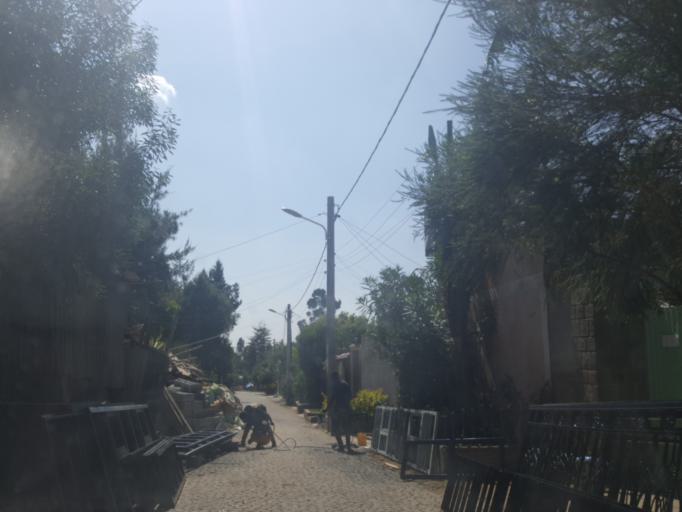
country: ET
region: Adis Abeba
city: Addis Ababa
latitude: 9.0664
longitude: 38.7161
